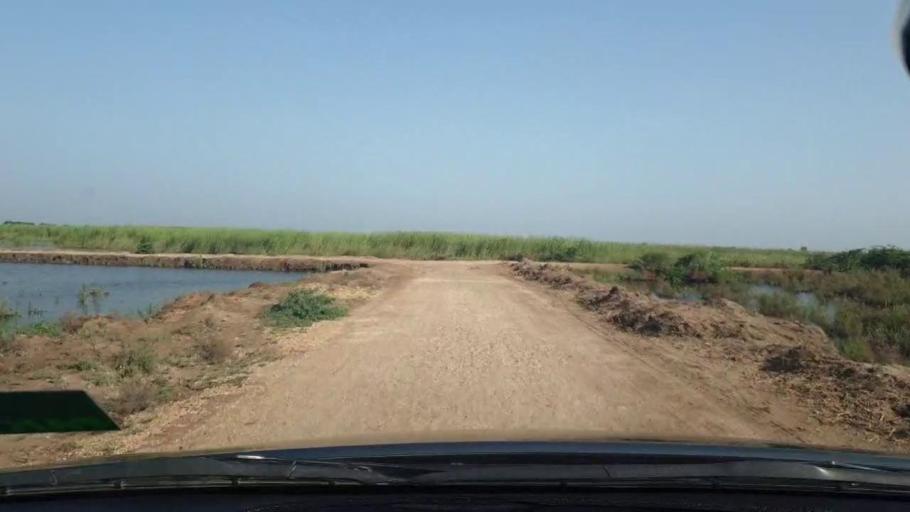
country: PK
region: Sindh
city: Tando Bago
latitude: 24.7230
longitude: 68.9533
